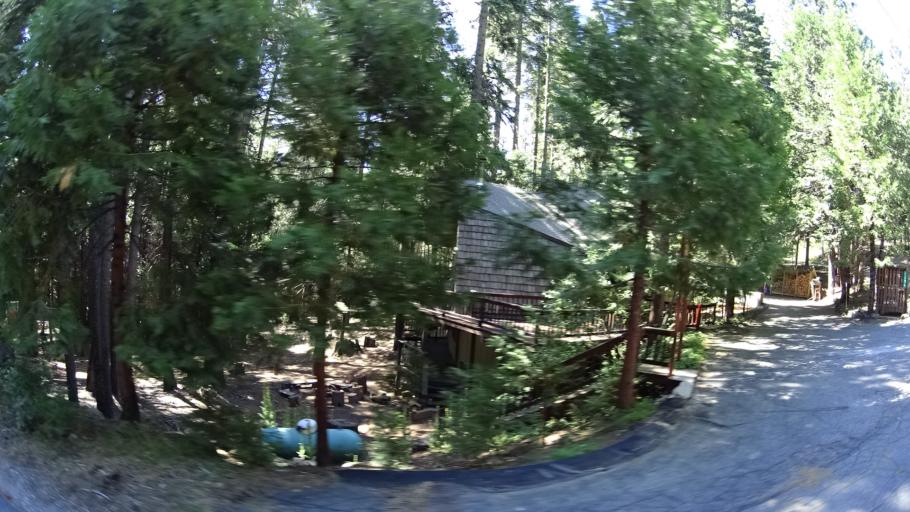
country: US
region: California
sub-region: Calaveras County
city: Arnold
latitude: 38.2809
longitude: -120.2809
